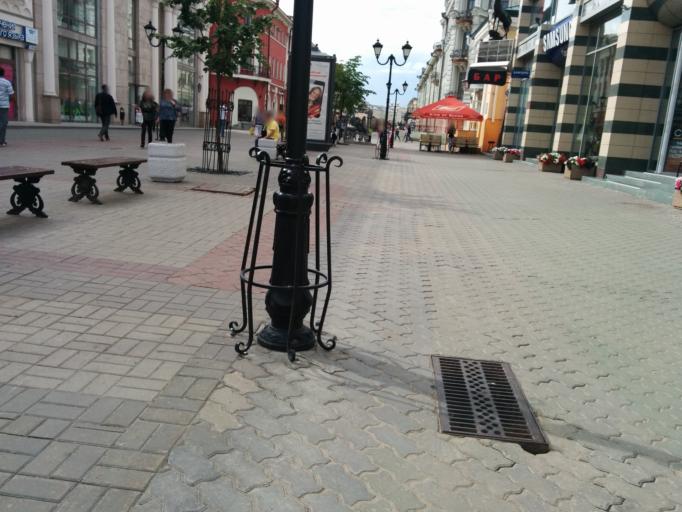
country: RU
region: Tatarstan
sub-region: Gorod Kazan'
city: Kazan
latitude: 55.7918
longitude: 49.1129
